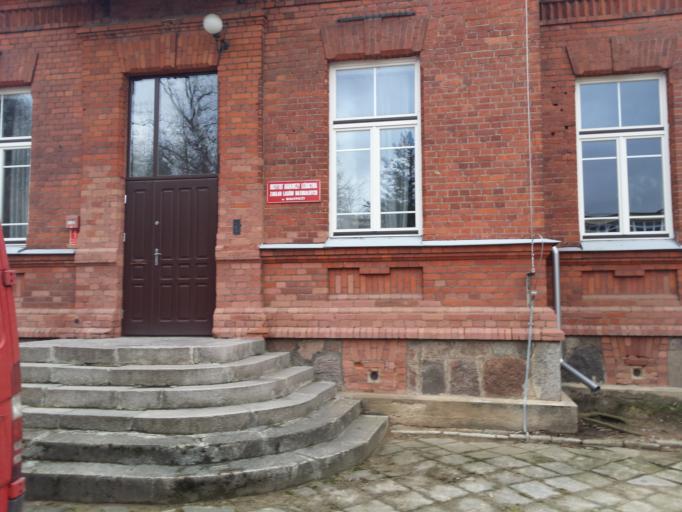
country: PL
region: Podlasie
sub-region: Powiat hajnowski
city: Bialowieza
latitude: 52.7023
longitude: 23.8747
